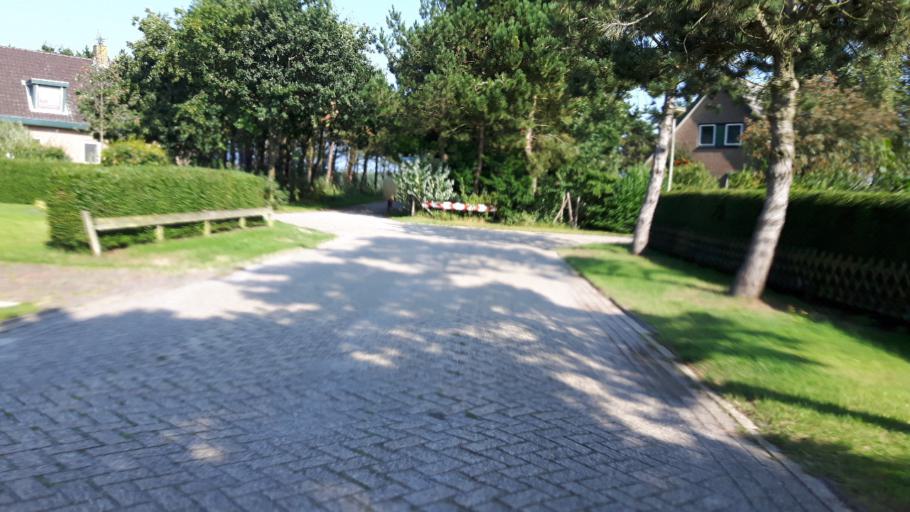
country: NL
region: Friesland
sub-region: Gemeente Ameland
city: Nes
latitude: 53.4493
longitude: 5.7961
